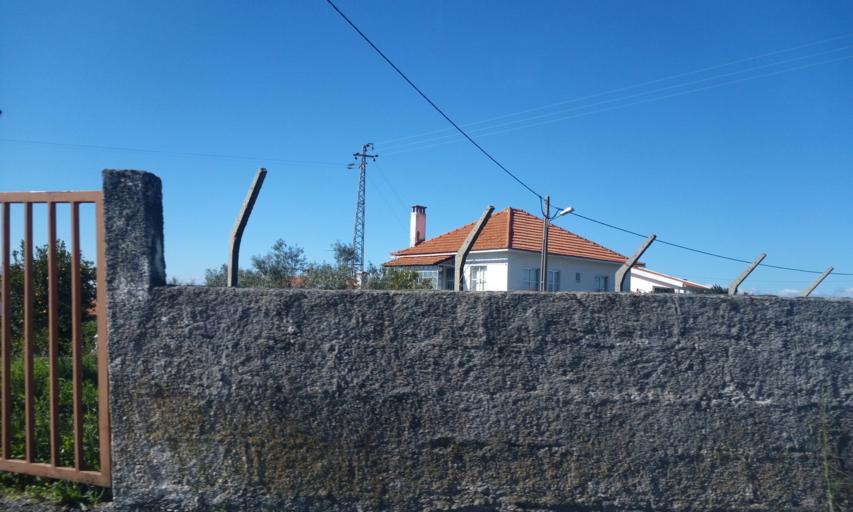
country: PT
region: Guarda
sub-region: Seia
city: Seia
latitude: 40.4674
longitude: -7.6208
